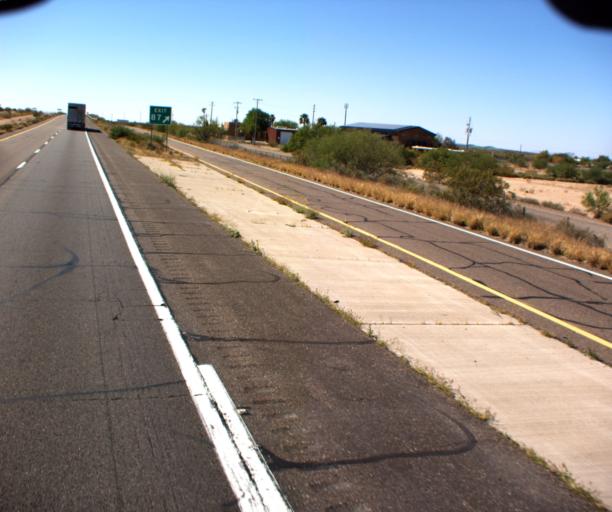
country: US
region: Arizona
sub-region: Maricopa County
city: Gila Bend
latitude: 32.8591
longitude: -113.2087
